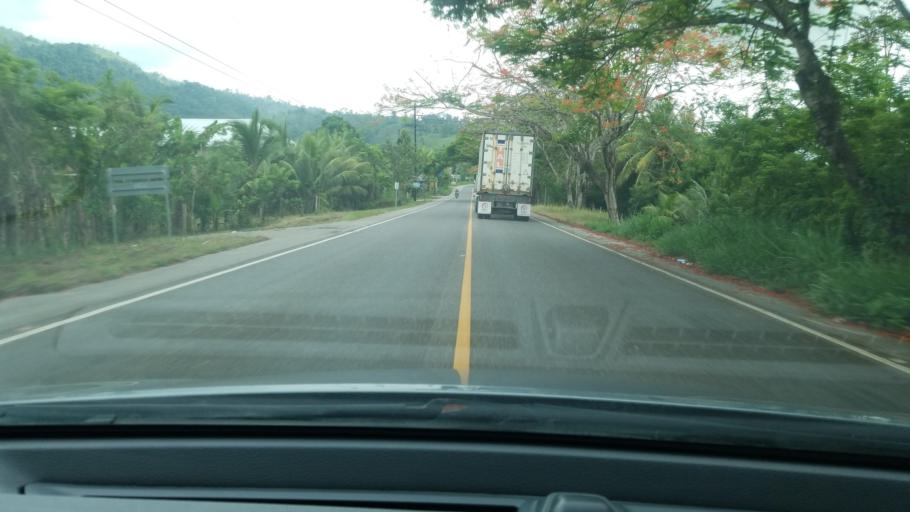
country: HN
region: Cortes
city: Potrerillos
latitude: 15.5888
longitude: -88.3284
